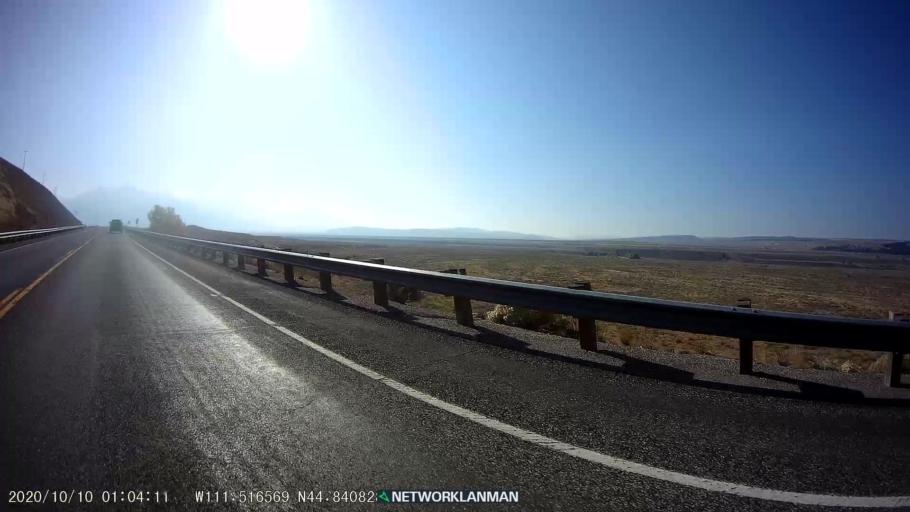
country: US
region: Montana
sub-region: Gallatin County
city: West Yellowstone
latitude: 44.8407
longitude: -111.5163
